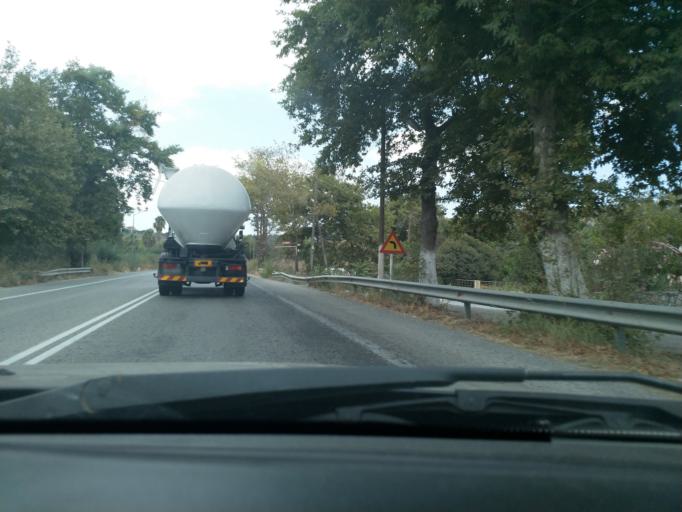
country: GR
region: Crete
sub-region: Nomos Chanias
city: Georgioupolis
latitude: 35.3816
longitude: 24.1986
